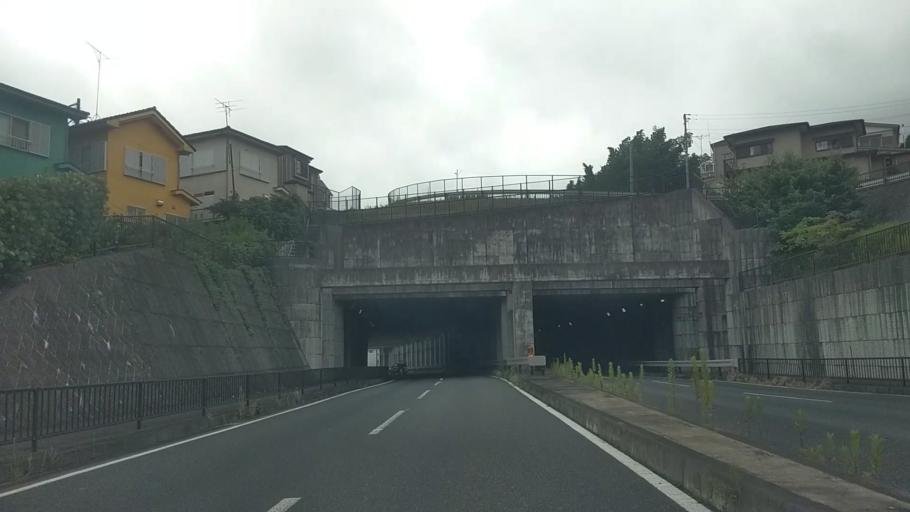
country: JP
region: Kanagawa
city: Yokosuka
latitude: 35.2611
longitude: 139.6410
